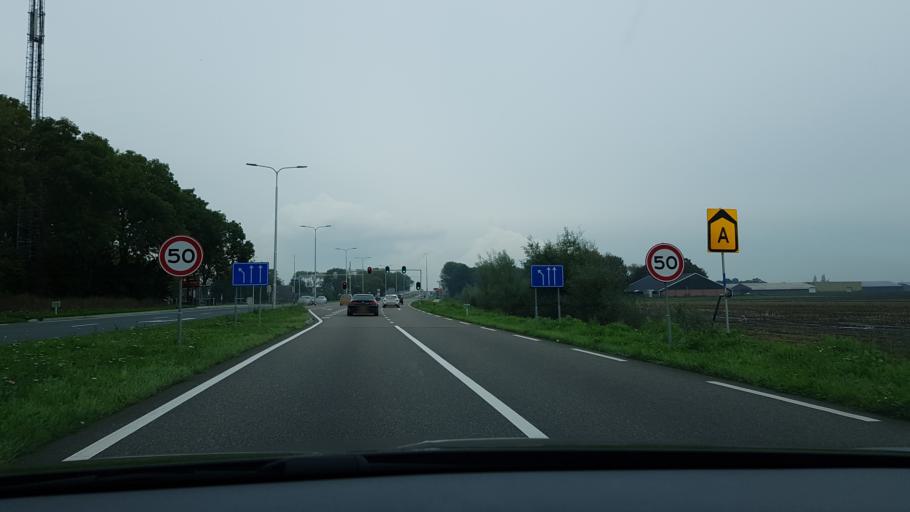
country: NL
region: South Holland
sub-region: Gemeente Kaag en Braassem
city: Leimuiden
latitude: 52.1857
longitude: 4.6734
